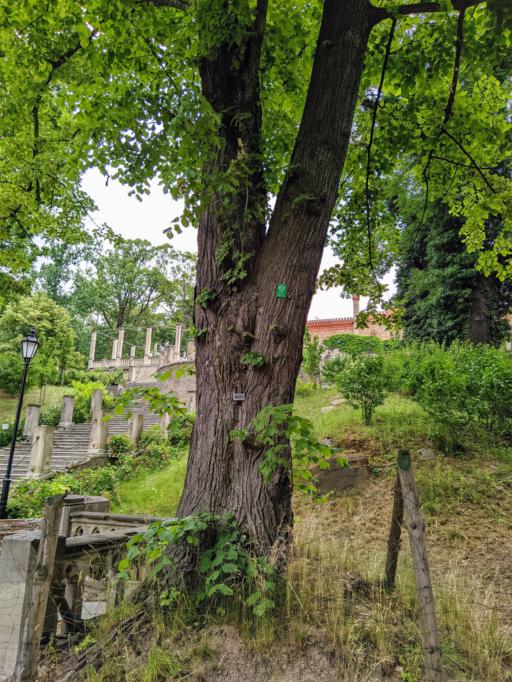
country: PL
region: Lower Silesian Voivodeship
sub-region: Powiat zabkowicki
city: Kamieniec Zabkowicki
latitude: 50.5201
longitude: 16.8792
